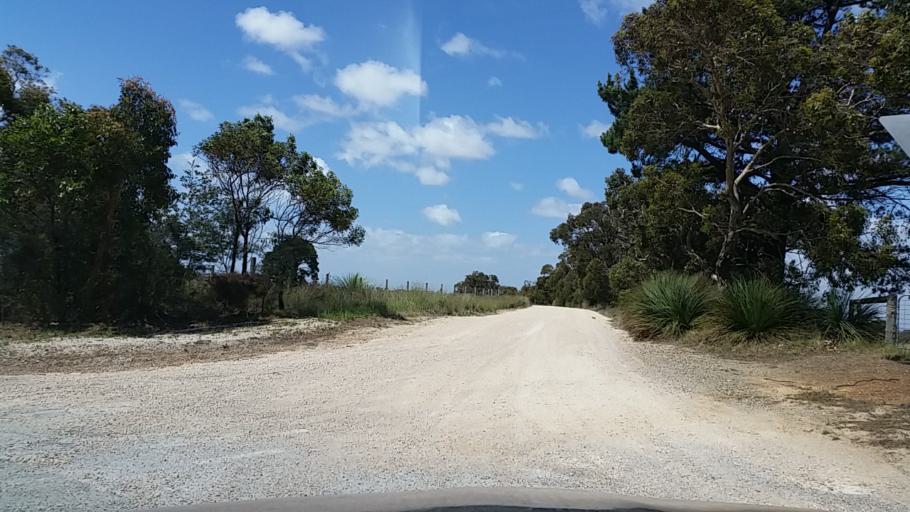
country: AU
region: South Australia
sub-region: Alexandrina
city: Port Elliot
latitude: -35.4537
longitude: 138.6439
